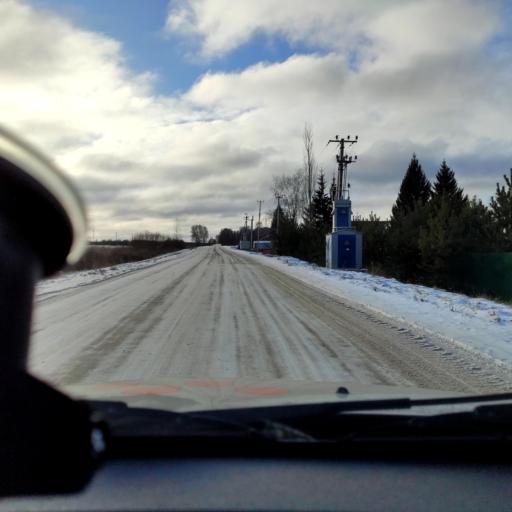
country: RU
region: Bashkortostan
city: Mikhaylovka
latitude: 54.7895
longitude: 55.7622
